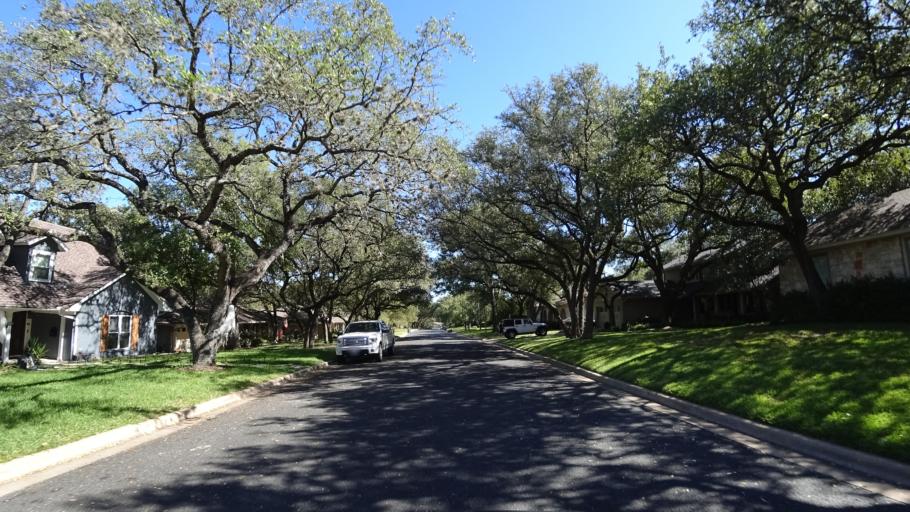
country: US
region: Texas
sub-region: Travis County
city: West Lake Hills
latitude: 30.3628
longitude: -97.7591
